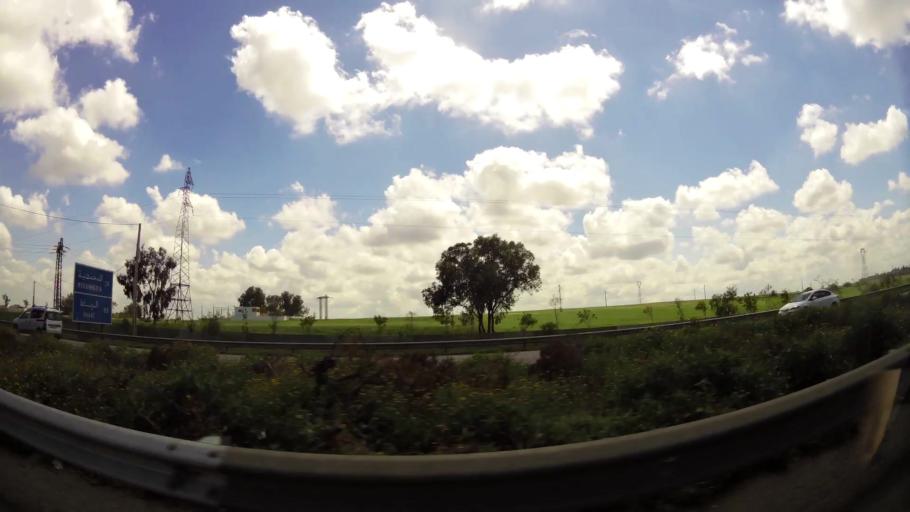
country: MA
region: Grand Casablanca
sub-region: Casablanca
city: Casablanca
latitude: 33.5131
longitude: -7.6015
